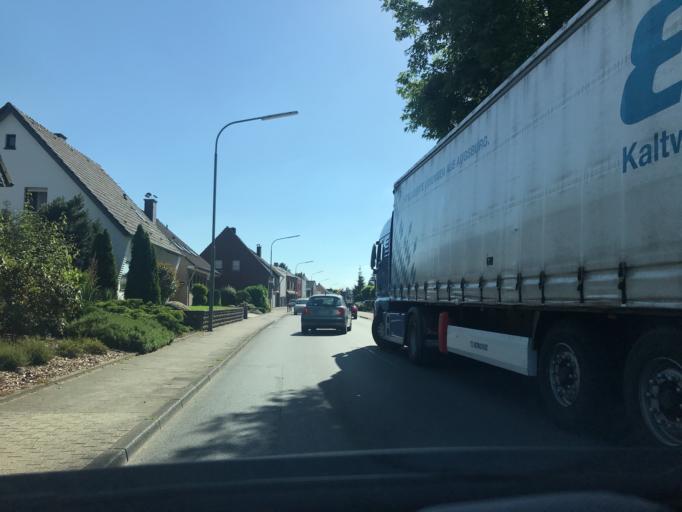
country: DE
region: North Rhine-Westphalia
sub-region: Regierungsbezirk Dusseldorf
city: Neuss
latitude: 51.1275
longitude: 6.7370
